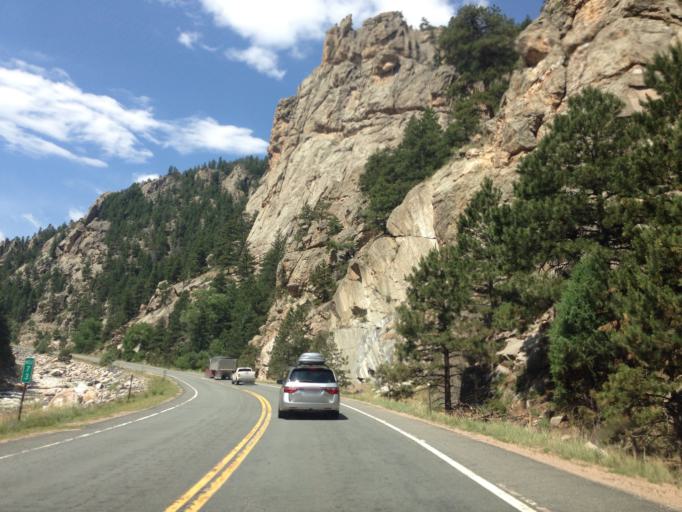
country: US
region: Colorado
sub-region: Larimer County
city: Estes Park
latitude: 40.4164
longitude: -105.3726
